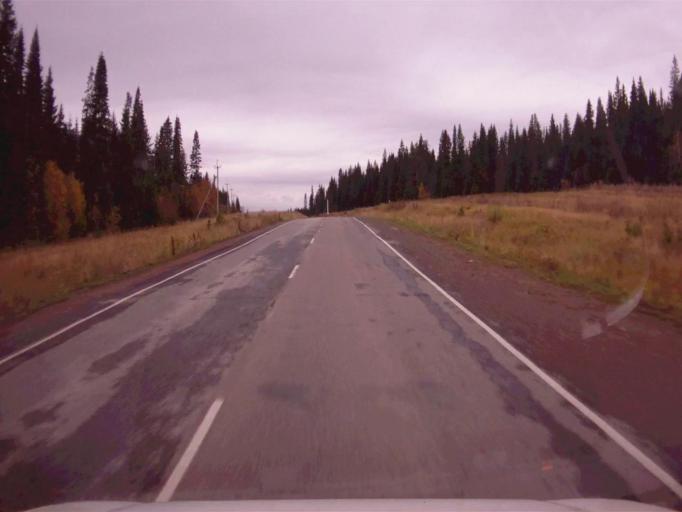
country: RU
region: Chelyabinsk
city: Nyazepetrovsk
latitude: 56.0662
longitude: 59.6374
